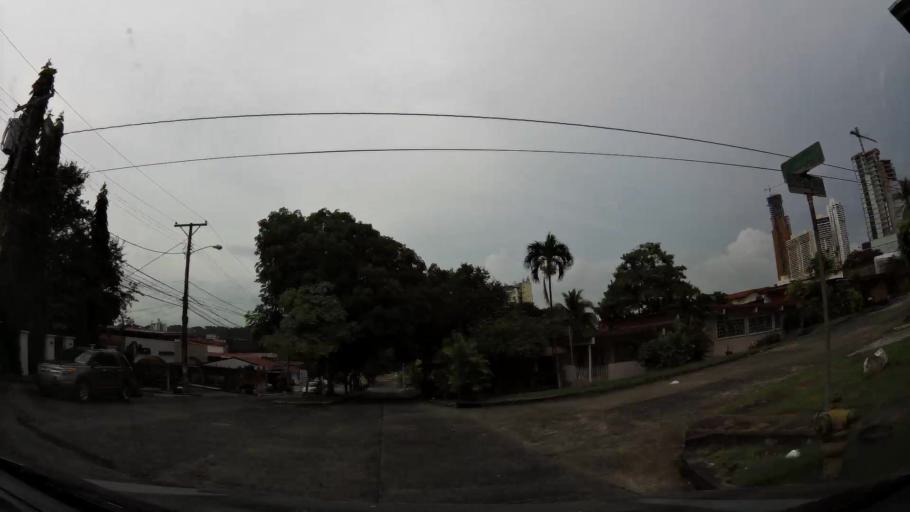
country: PA
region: Panama
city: Panama
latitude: 8.9979
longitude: -79.5317
